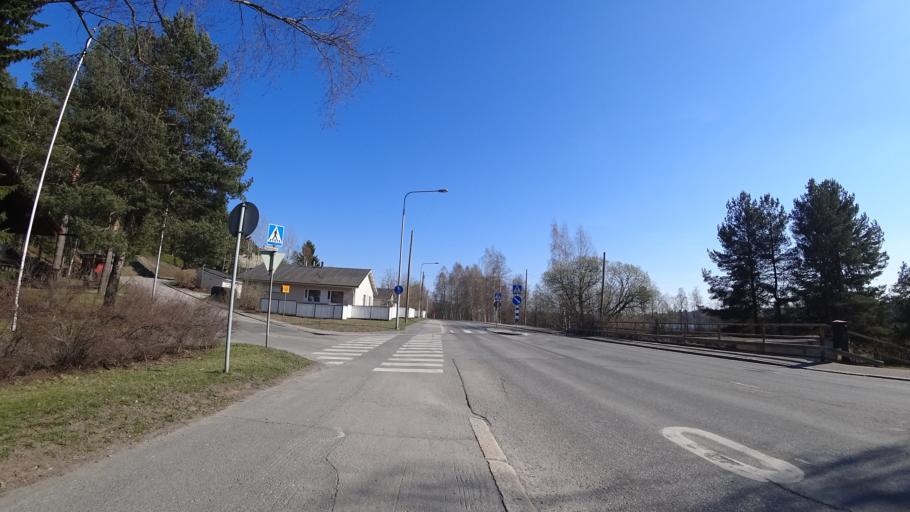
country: FI
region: Pirkanmaa
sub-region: Tampere
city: Pirkkala
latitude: 61.5144
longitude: 23.6529
